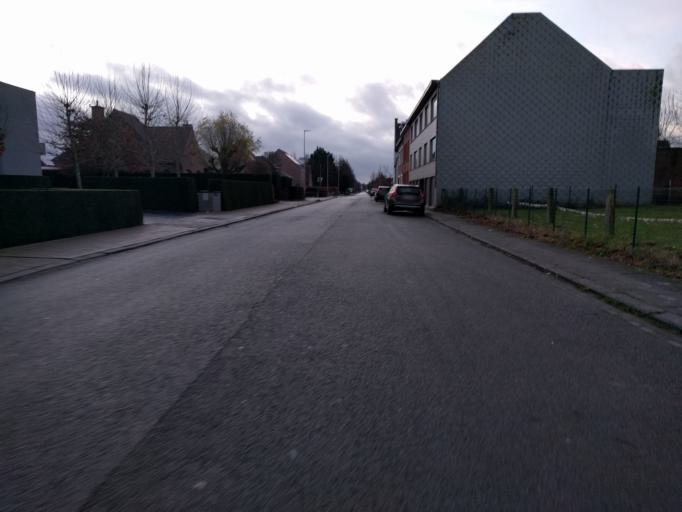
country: BE
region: Flanders
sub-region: Provincie West-Vlaanderen
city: Wevelgem
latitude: 50.8155
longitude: 3.1684
